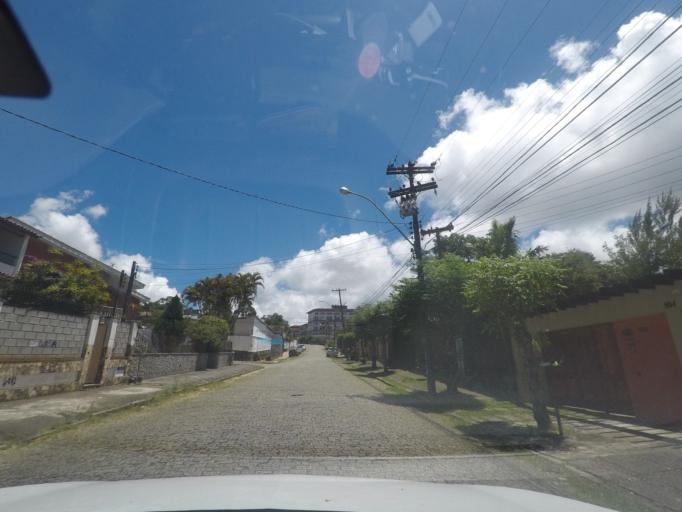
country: BR
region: Rio de Janeiro
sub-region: Teresopolis
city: Teresopolis
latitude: -22.4360
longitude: -42.9823
